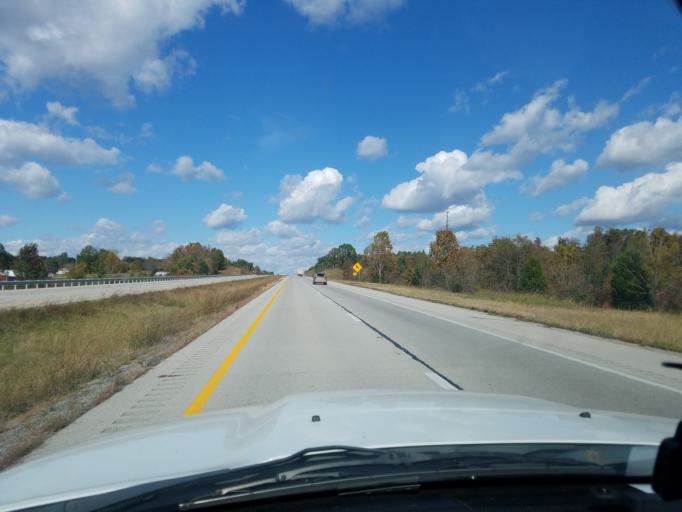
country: US
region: Kentucky
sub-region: Ohio County
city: Hartford
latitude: 37.5181
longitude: -86.9183
